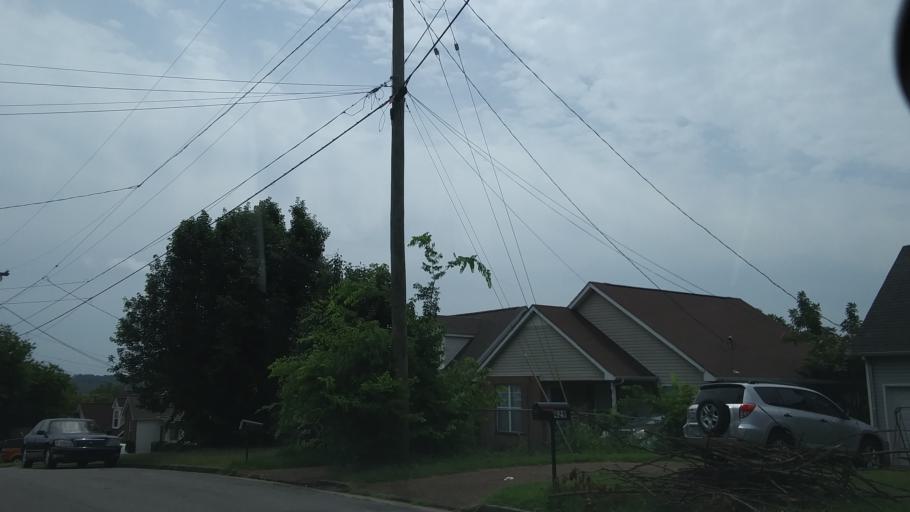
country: US
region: Tennessee
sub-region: Davidson County
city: Belle Meade
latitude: 36.1521
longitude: -86.8650
